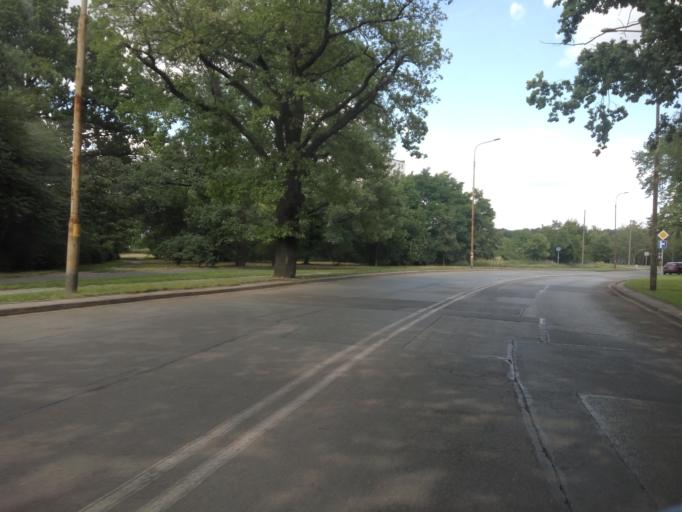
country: PL
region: Lower Silesian Voivodeship
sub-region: Powiat wroclawski
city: Wroclaw
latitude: 51.1346
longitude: 16.9758
